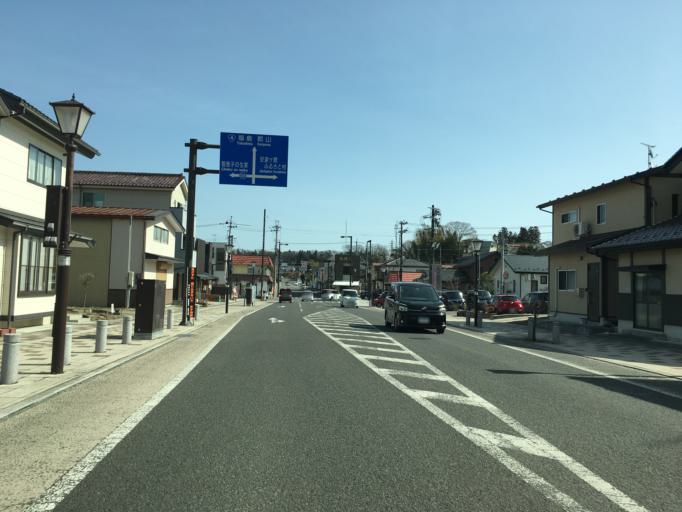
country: JP
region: Fukushima
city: Nihommatsu
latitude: 37.5993
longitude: 140.4478
